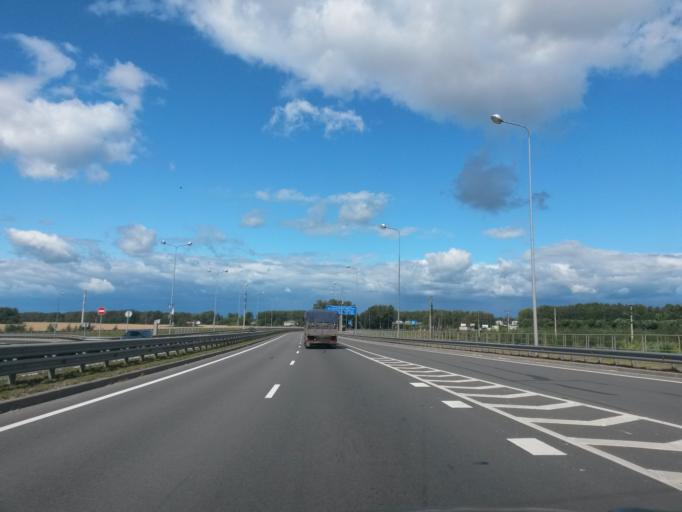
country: RU
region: Jaroslavl
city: Yaroslavl
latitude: 57.6882
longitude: 39.9008
